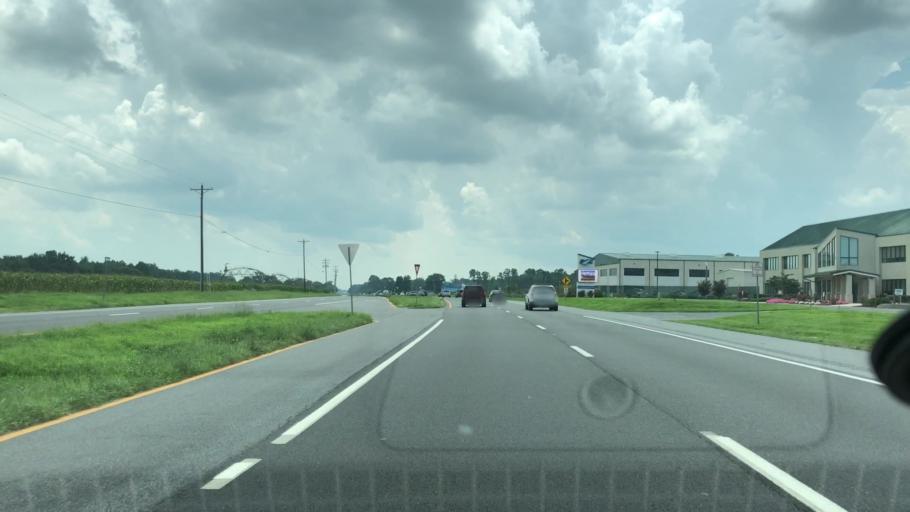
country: US
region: Delaware
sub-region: Sussex County
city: Bridgeville
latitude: 38.7918
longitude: -75.5904
